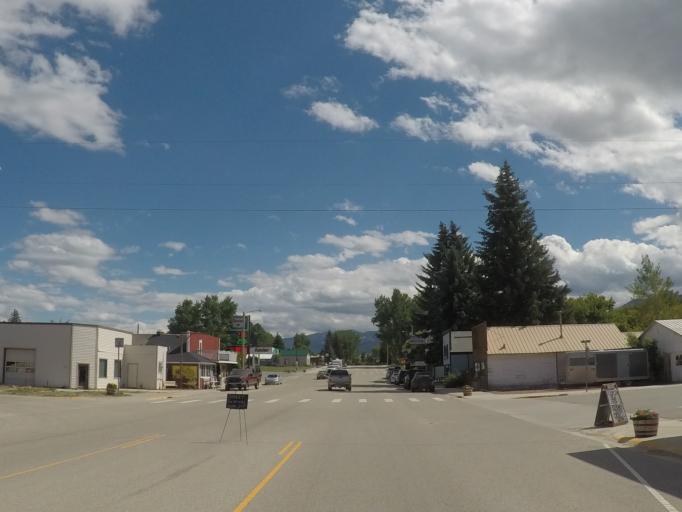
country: US
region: Wyoming
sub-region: Sheridan County
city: Sheridan
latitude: 44.8765
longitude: -107.2628
